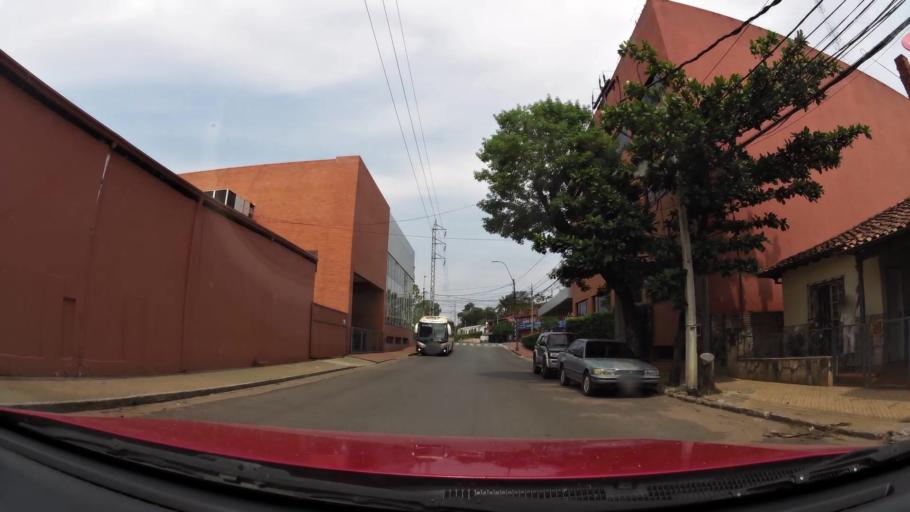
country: PY
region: Asuncion
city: Asuncion
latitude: -25.2919
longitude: -57.5758
